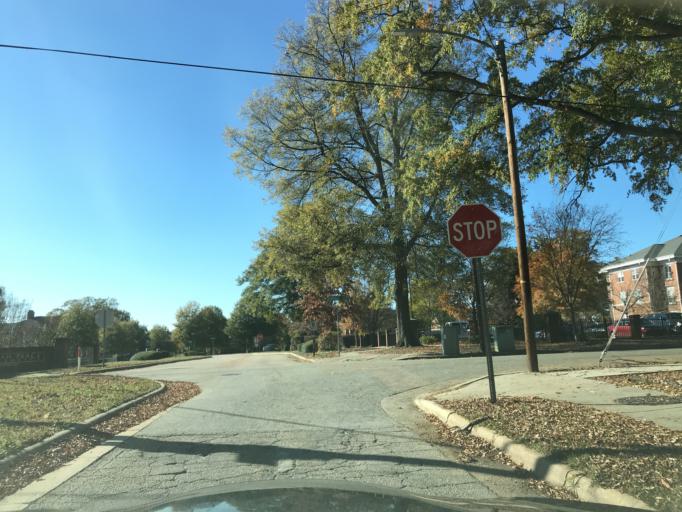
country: US
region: North Carolina
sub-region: Wake County
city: Raleigh
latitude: 35.7913
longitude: -78.6356
